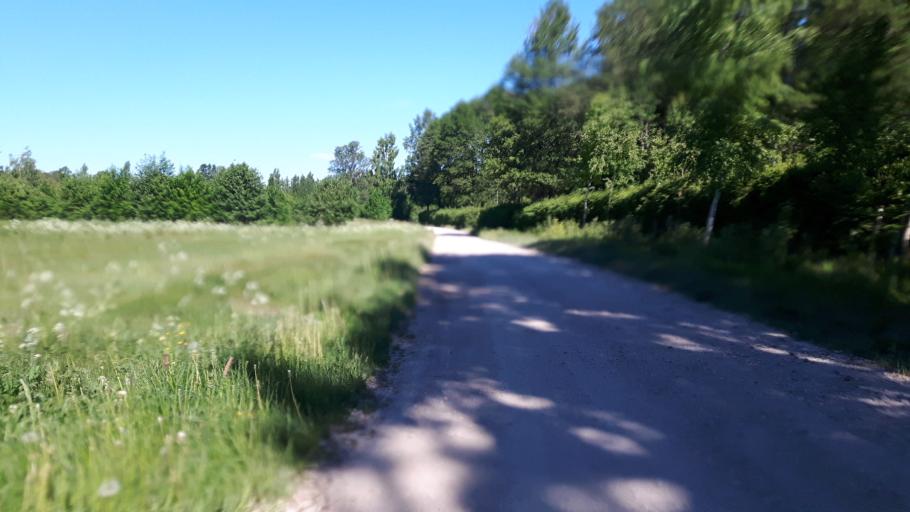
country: EE
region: Harju
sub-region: Loksa linn
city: Loksa
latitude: 59.5661
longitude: 25.8562
